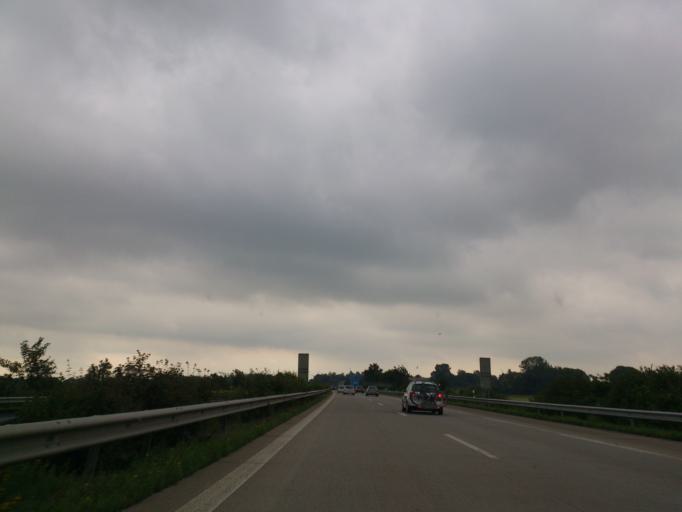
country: DE
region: Schleswig-Holstein
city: Rethwisch
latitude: 53.8496
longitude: 9.5875
